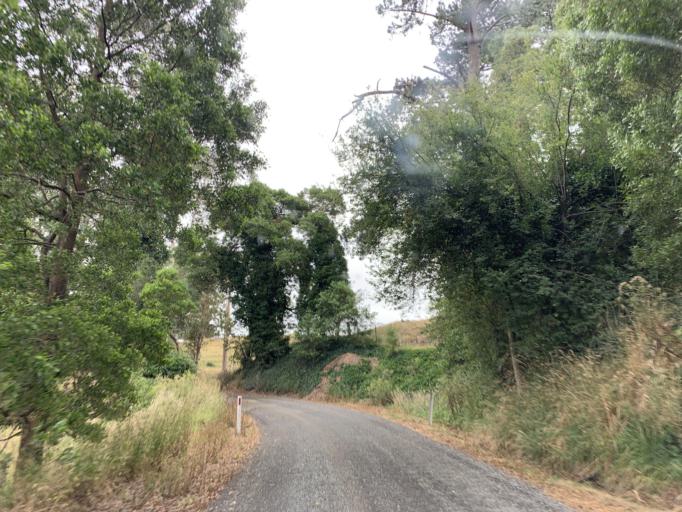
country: AU
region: Victoria
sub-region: Baw Baw
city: Warragul
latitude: -38.3250
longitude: 145.8372
